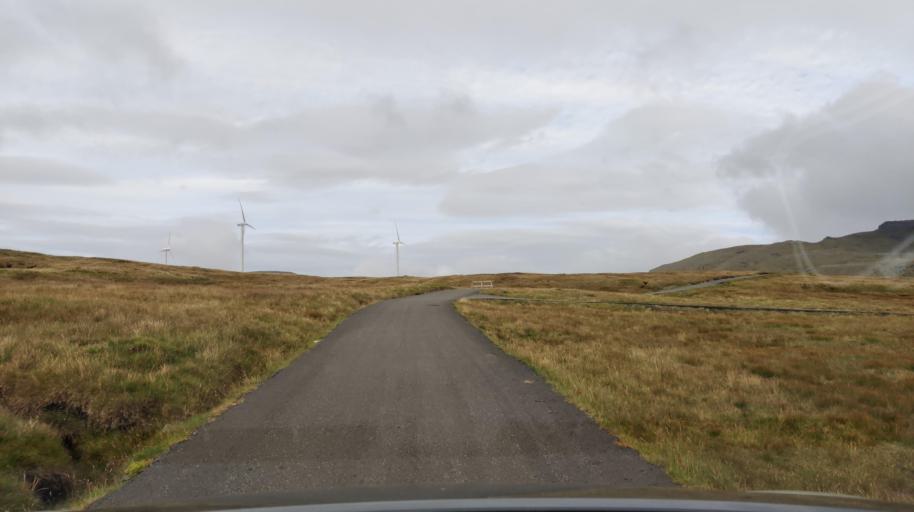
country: FO
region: Streymoy
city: Vestmanna
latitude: 62.1603
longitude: -7.1026
